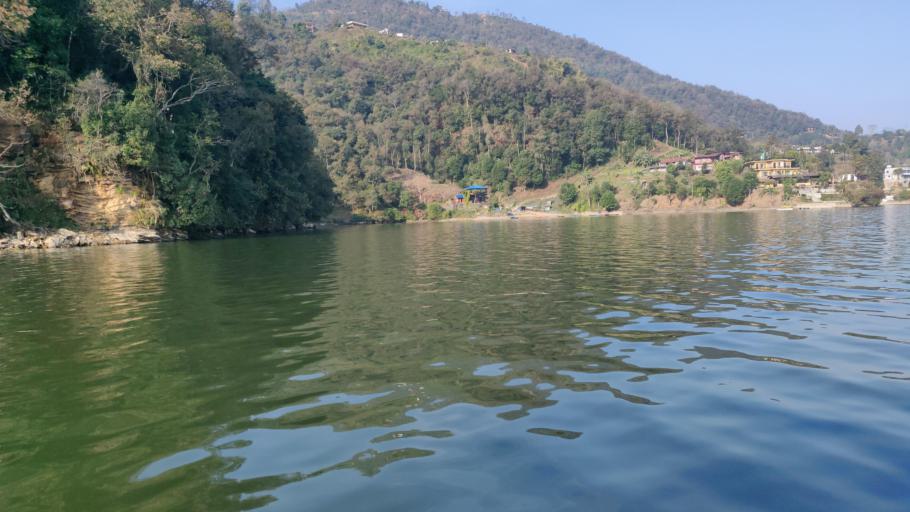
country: NP
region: Western Region
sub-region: Gandaki Zone
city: Pokhara
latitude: 28.2071
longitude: 83.9507
